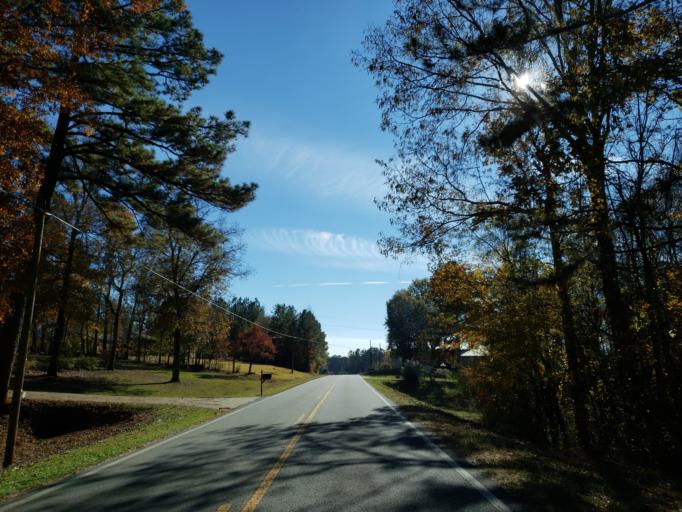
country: US
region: Alabama
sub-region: Cleburne County
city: Heflin
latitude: 33.5839
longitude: -85.6385
